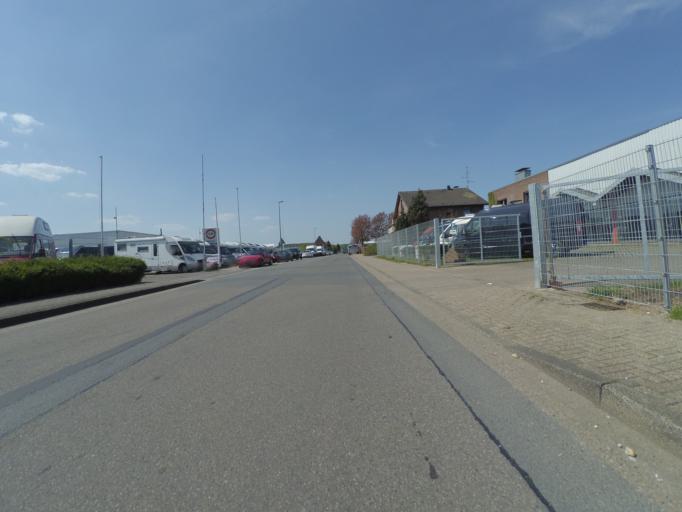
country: DE
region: North Rhine-Westphalia
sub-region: Regierungsbezirk Dusseldorf
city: Emmerich
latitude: 51.8336
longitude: 6.2750
